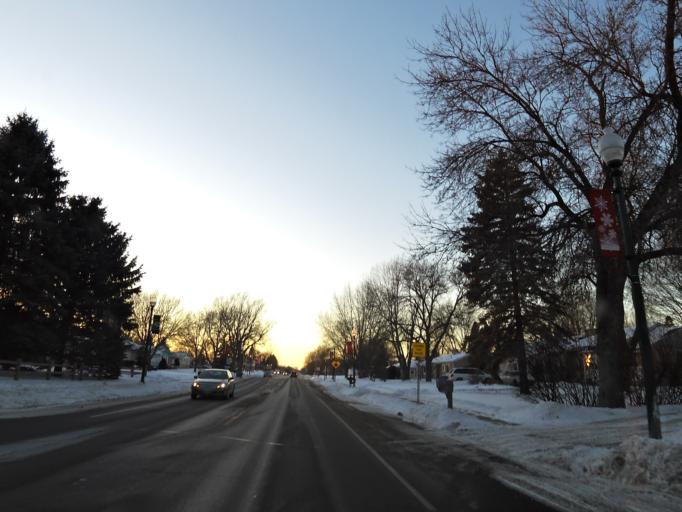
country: US
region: Minnesota
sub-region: Dakota County
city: Rosemount
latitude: 44.7392
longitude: -93.1338
